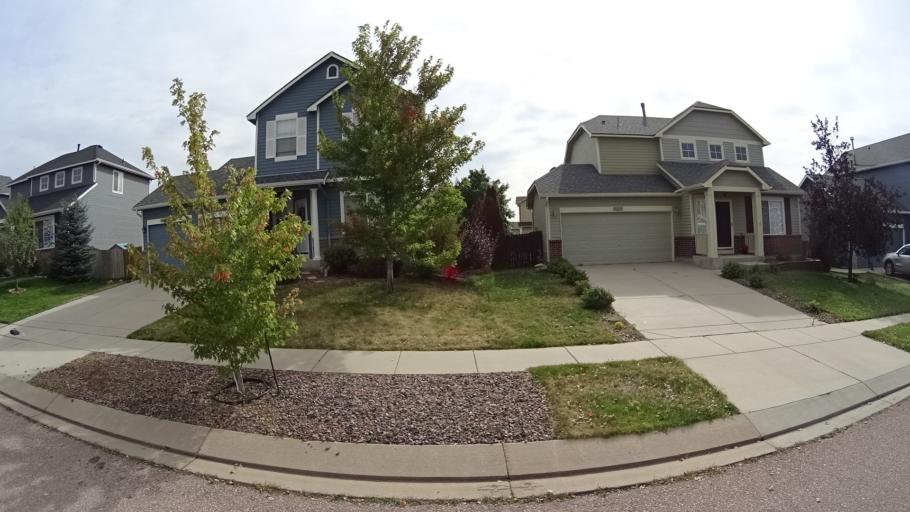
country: US
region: Colorado
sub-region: El Paso County
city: Cimarron Hills
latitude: 38.9226
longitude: -104.7133
